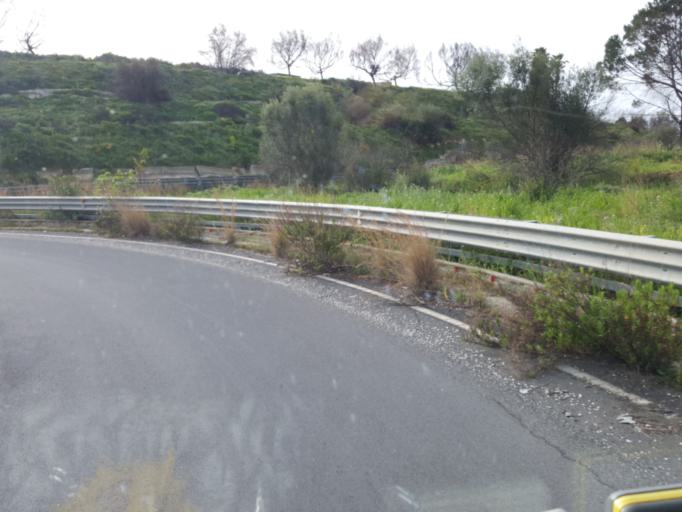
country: IT
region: Sicily
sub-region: Provincia di Siracusa
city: Melilli
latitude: 37.2163
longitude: 15.1542
